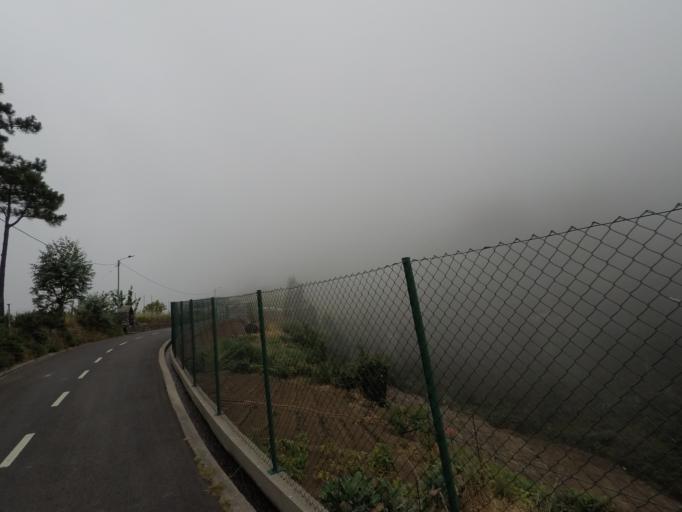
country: PT
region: Madeira
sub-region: Camara de Lobos
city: Curral das Freiras
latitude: 32.6897
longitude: -16.9475
